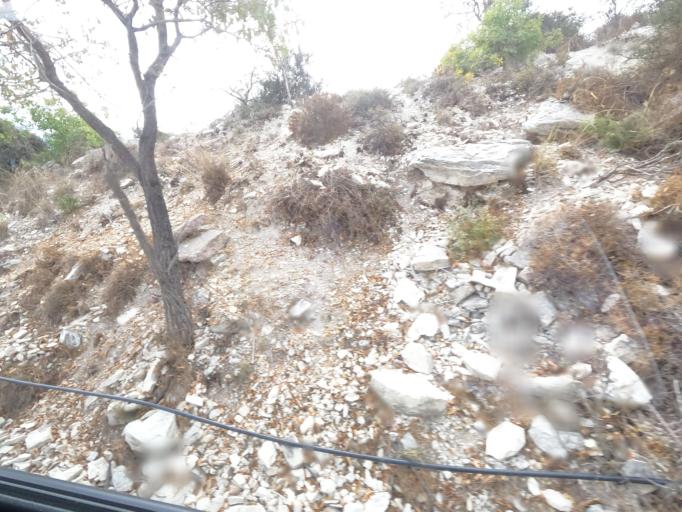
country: CY
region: Pafos
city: Mesogi
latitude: 34.8163
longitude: 32.4655
